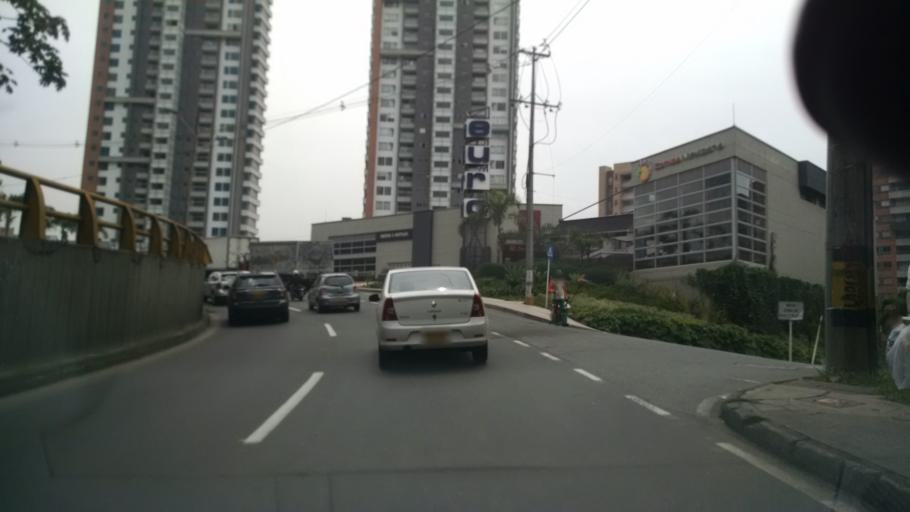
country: CO
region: Antioquia
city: Medellin
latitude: 6.2207
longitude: -75.5661
